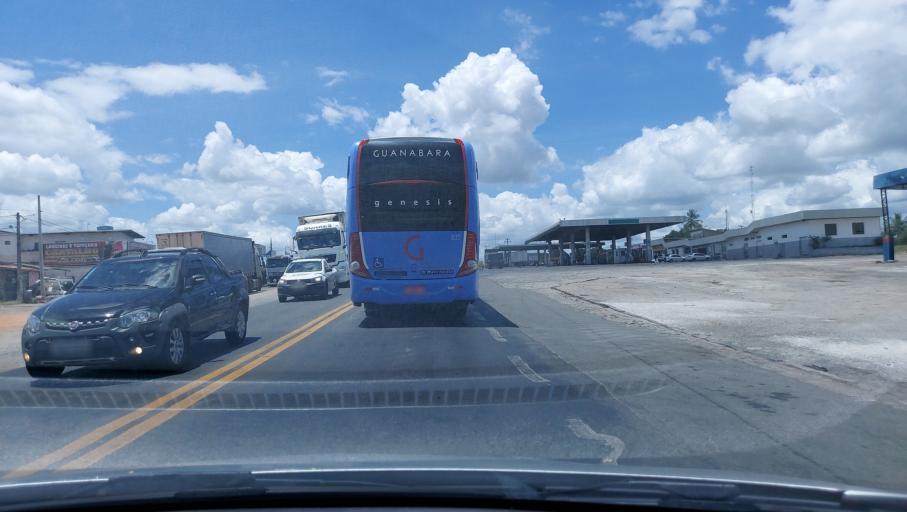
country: BR
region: Bahia
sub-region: Castro Alves
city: Castro Alves
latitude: -12.5812
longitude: -39.5170
